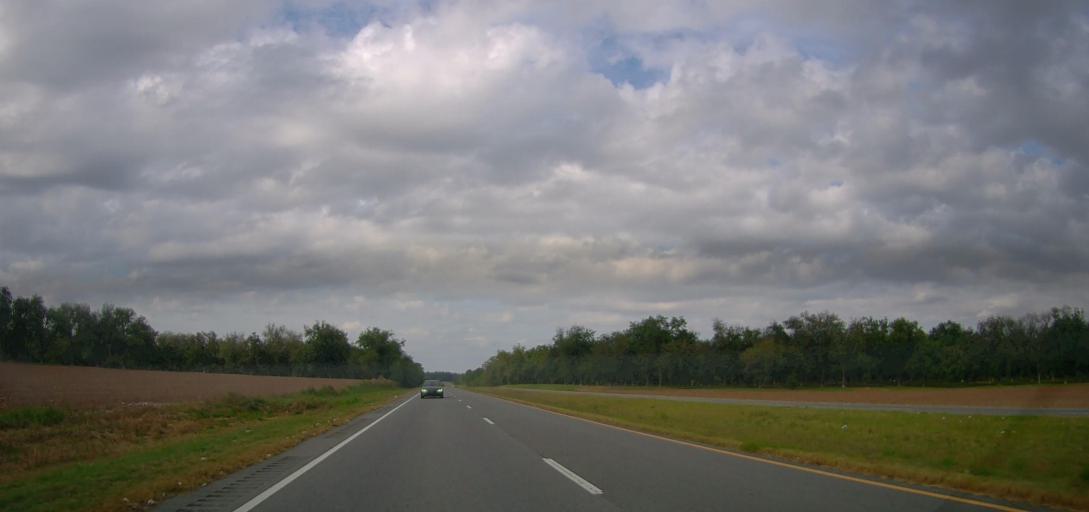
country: US
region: Georgia
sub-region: Thomas County
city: Meigs
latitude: 31.0337
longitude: -84.0641
